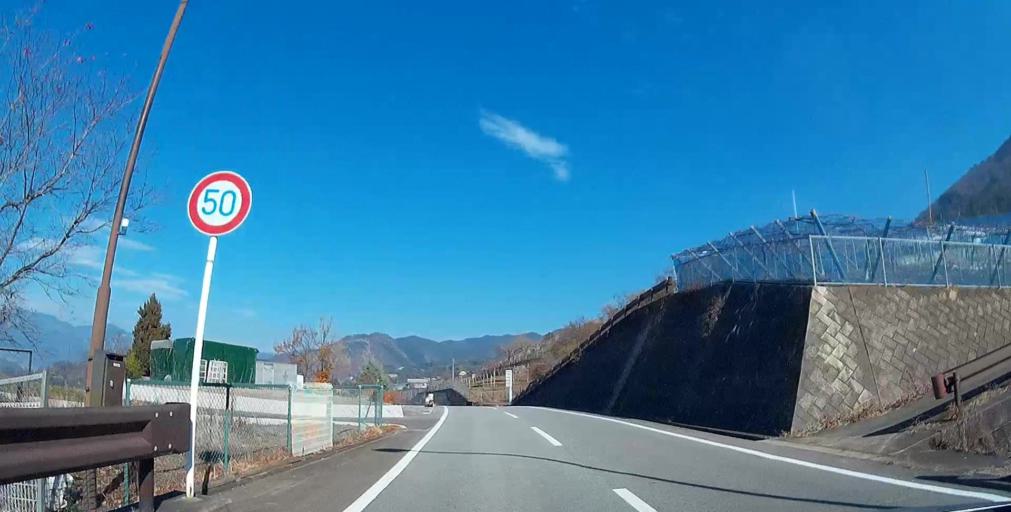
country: JP
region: Yamanashi
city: Enzan
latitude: 35.6705
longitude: 138.7454
